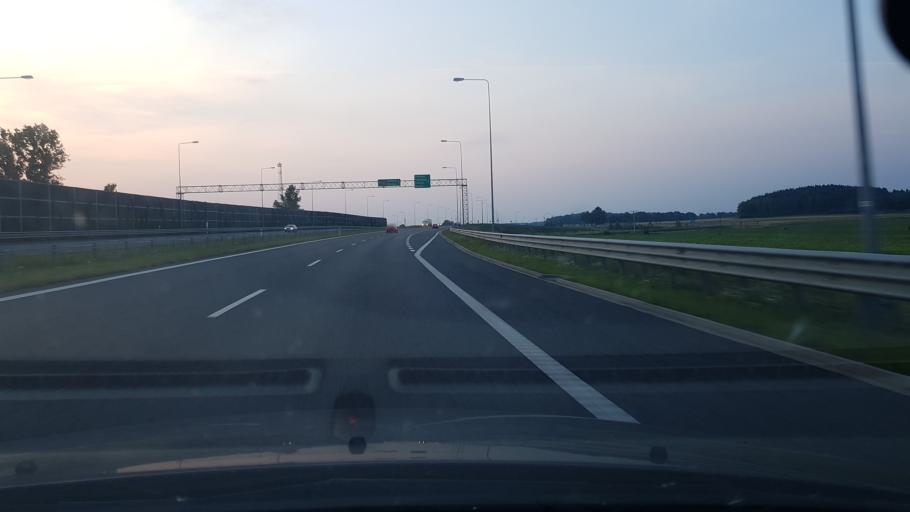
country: PL
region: Warmian-Masurian Voivodeship
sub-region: Powiat nidzicki
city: Nidzica
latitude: 53.4074
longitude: 20.3400
